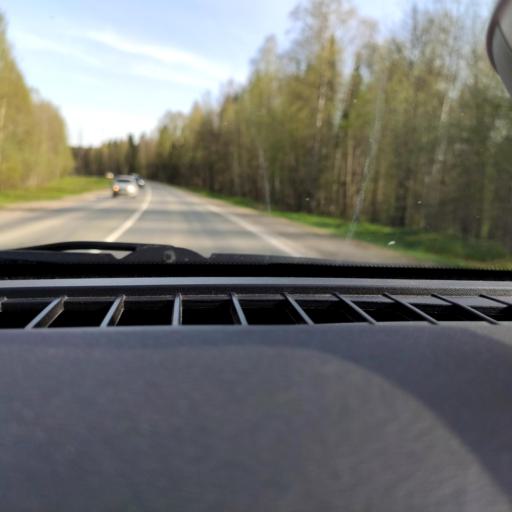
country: RU
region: Perm
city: Perm
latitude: 58.1419
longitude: 56.2668
